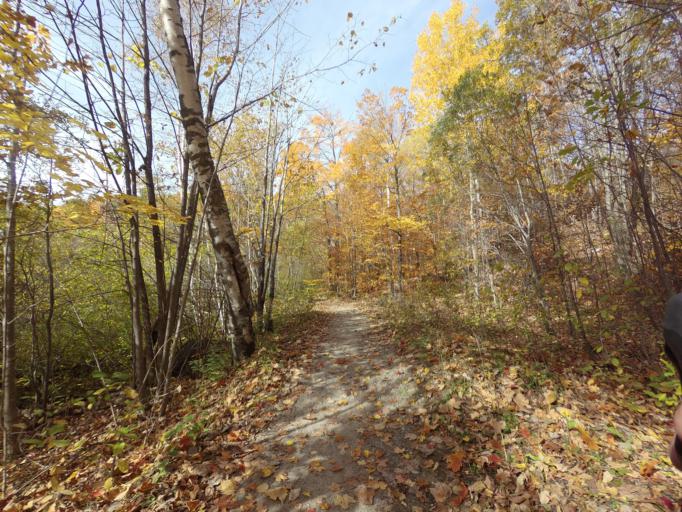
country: CA
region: Quebec
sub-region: Outaouais
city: Gatineau
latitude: 45.4713
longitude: -75.7955
